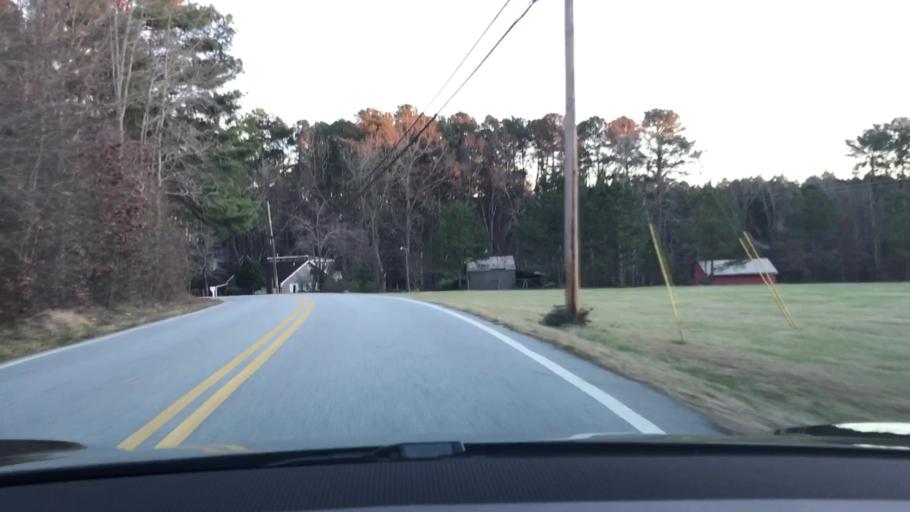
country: US
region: Georgia
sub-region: Gwinnett County
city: Grayson
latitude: 33.8885
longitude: -83.9195
